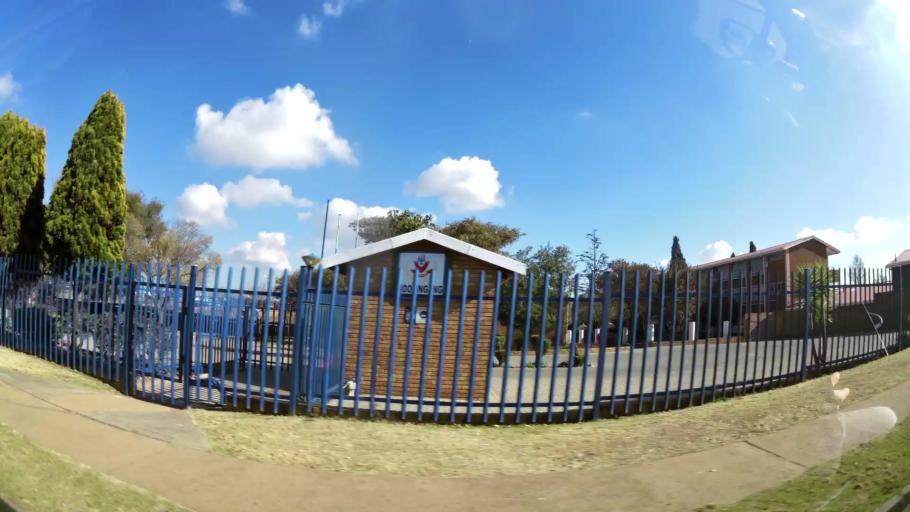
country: ZA
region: Gauteng
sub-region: City of Johannesburg Metropolitan Municipality
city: Roodepoort
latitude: -26.1501
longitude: 27.8222
